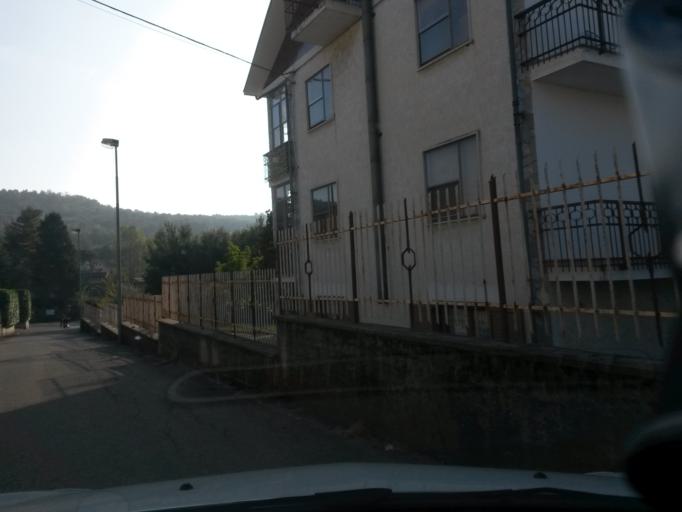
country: IT
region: Piedmont
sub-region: Provincia di Torino
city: Buttigliera Alta
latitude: 45.0695
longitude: 7.4264
